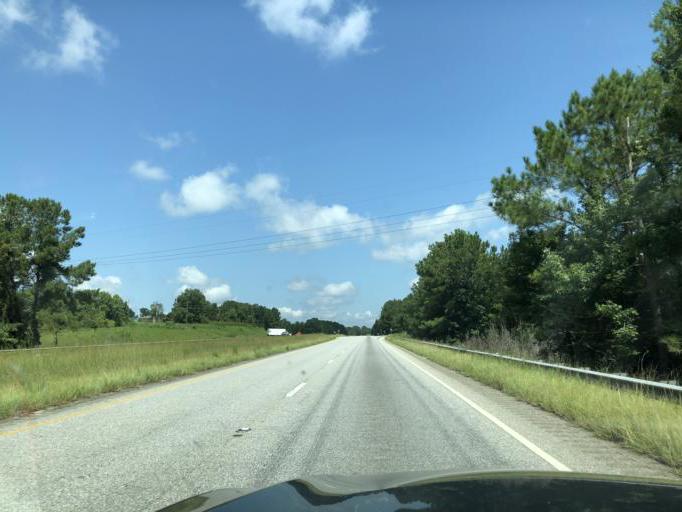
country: US
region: Alabama
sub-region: Henry County
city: Abbeville
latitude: 31.6872
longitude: -85.2788
